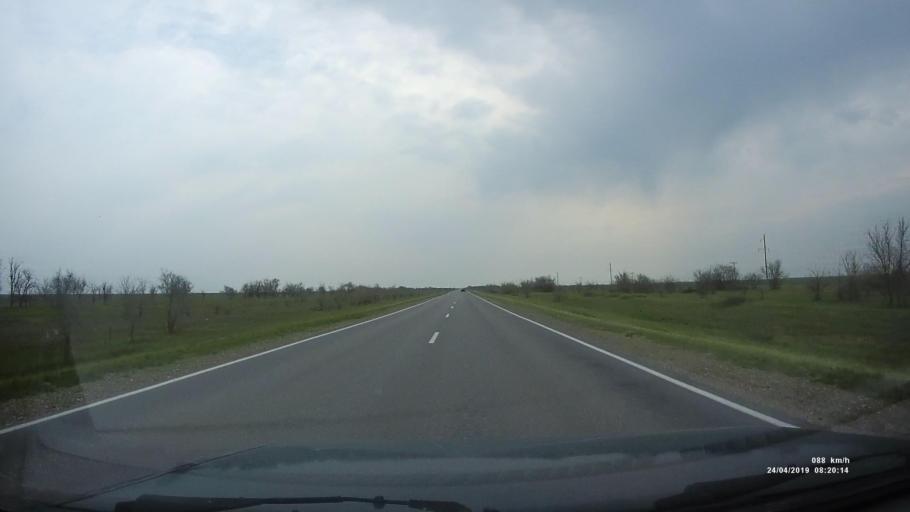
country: RU
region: Kalmykiya
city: Priyutnoye
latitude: 46.1067
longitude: 43.6794
